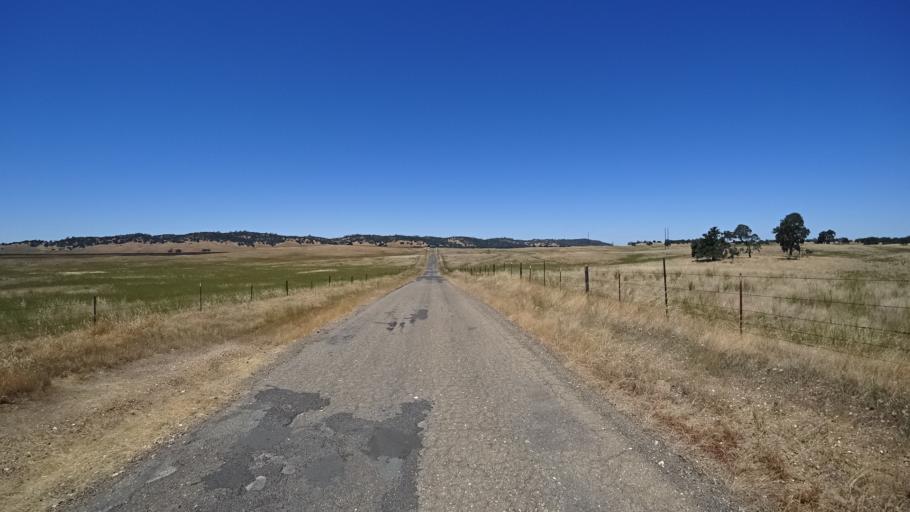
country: US
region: California
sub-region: Calaveras County
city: Rancho Calaveras
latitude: 38.0574
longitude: -120.7528
